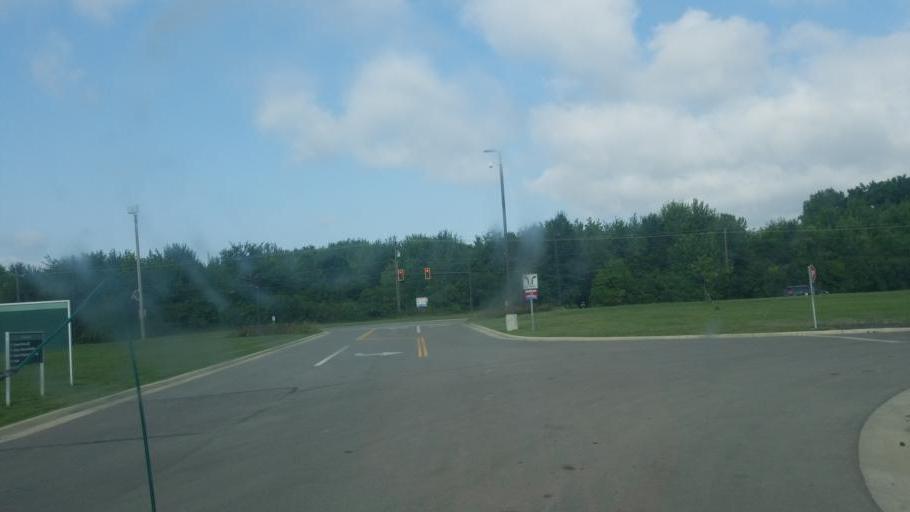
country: US
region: Ohio
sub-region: Marion County
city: Marion
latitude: 40.5765
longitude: -83.0918
